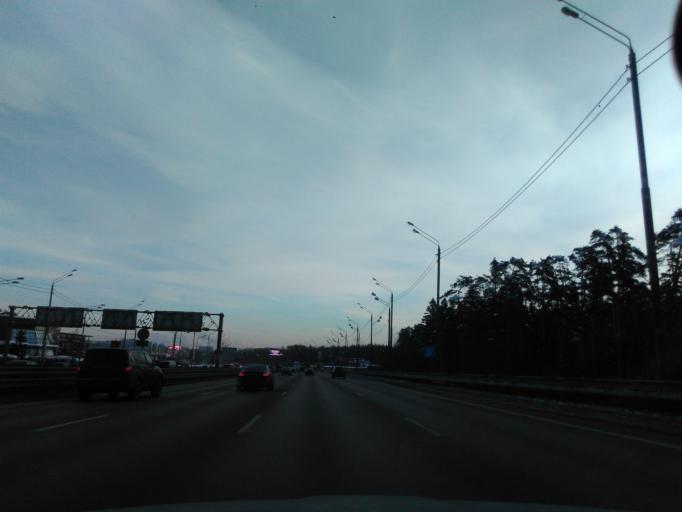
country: RU
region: Moskovskaya
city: Opalikha
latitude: 55.7866
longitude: 37.2511
